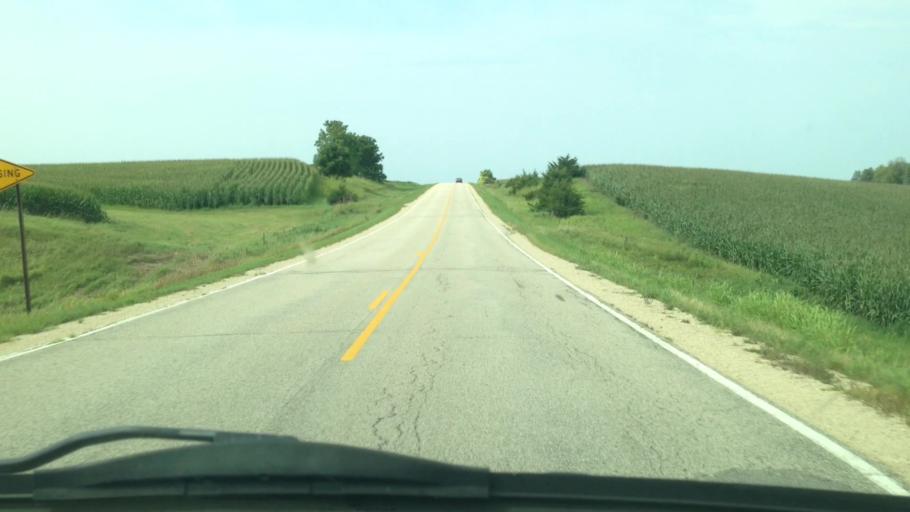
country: US
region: Minnesota
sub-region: Winona County
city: Saint Charles
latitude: 43.8663
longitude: -91.9594
